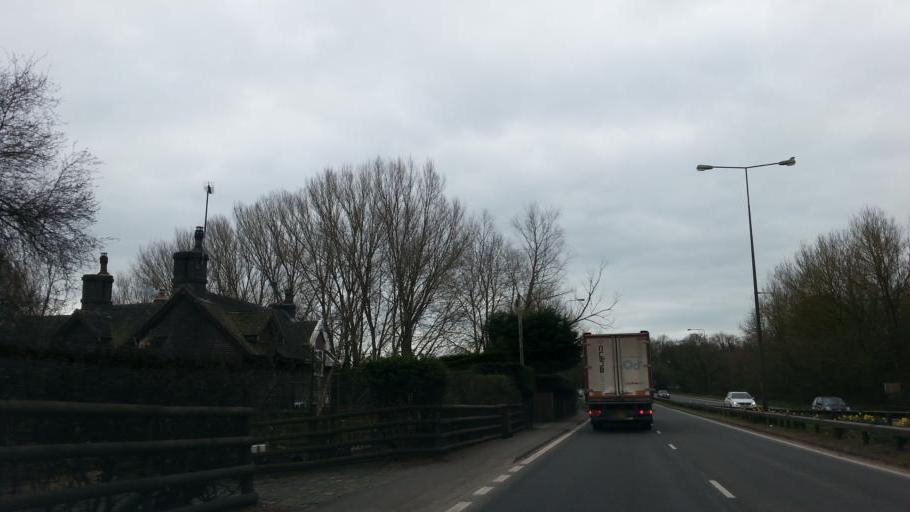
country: GB
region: England
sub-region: Staffordshire
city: Stone
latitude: 52.9061
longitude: -2.1612
